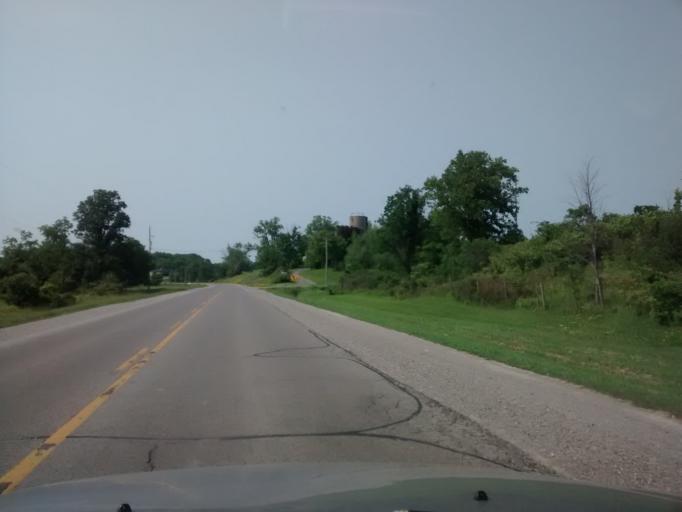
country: CA
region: Ontario
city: Ancaster
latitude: 43.0000
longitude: -79.8669
